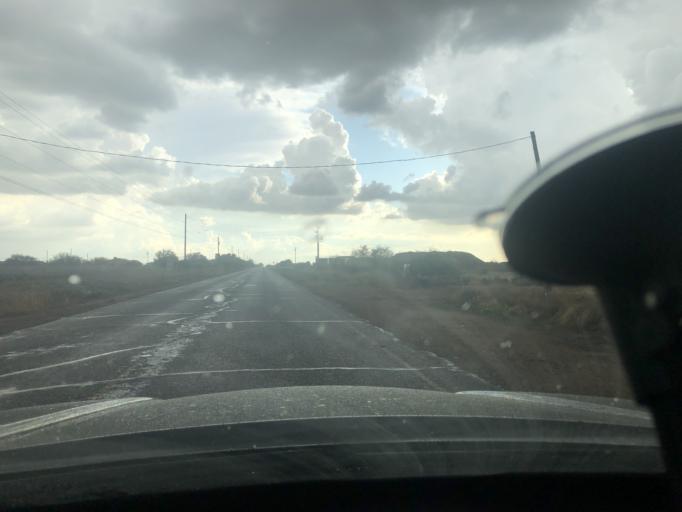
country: US
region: Arizona
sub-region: Maricopa County
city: Scottsdale
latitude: 33.4906
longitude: -111.8827
